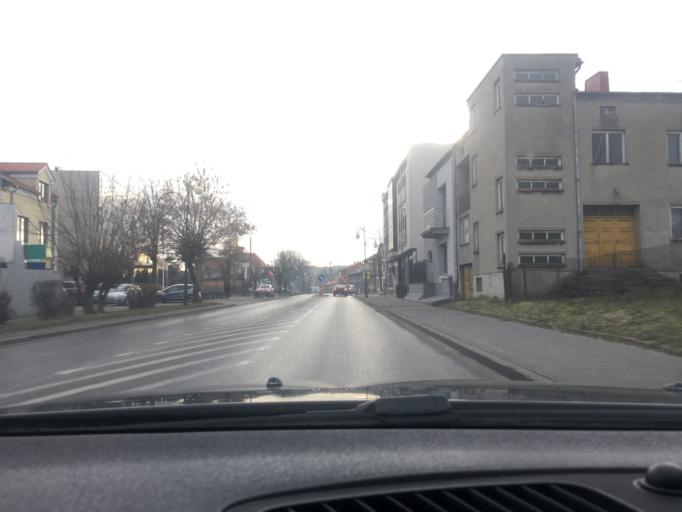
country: PL
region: Swietokrzyskie
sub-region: Powiat jedrzejowski
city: Jedrzejow
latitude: 50.6444
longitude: 20.2958
